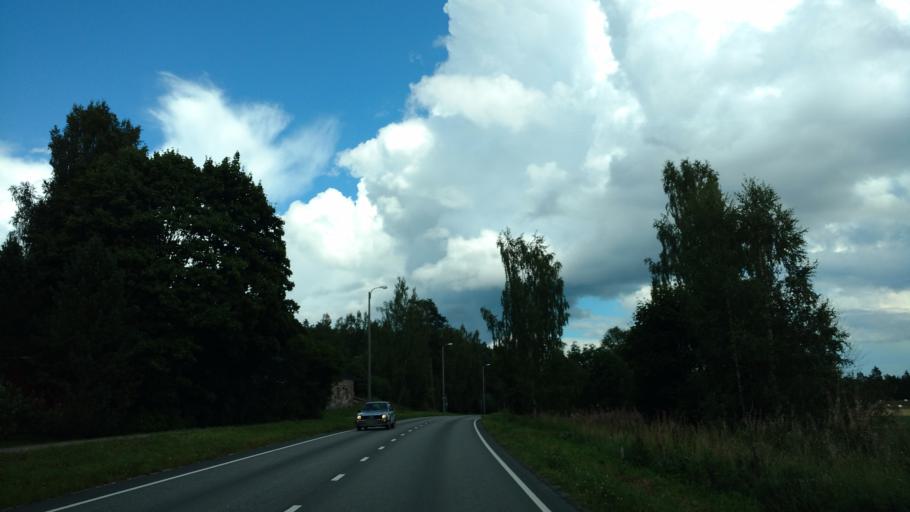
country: FI
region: Uusimaa
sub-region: Helsinki
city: Karjalohja
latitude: 60.2454
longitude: 23.7324
